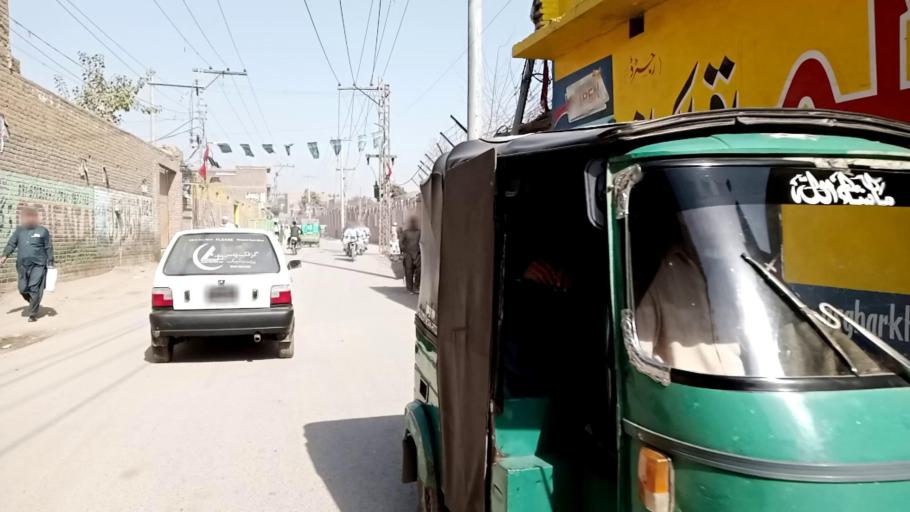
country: PK
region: Khyber Pakhtunkhwa
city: Peshawar
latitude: 33.9922
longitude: 71.5799
